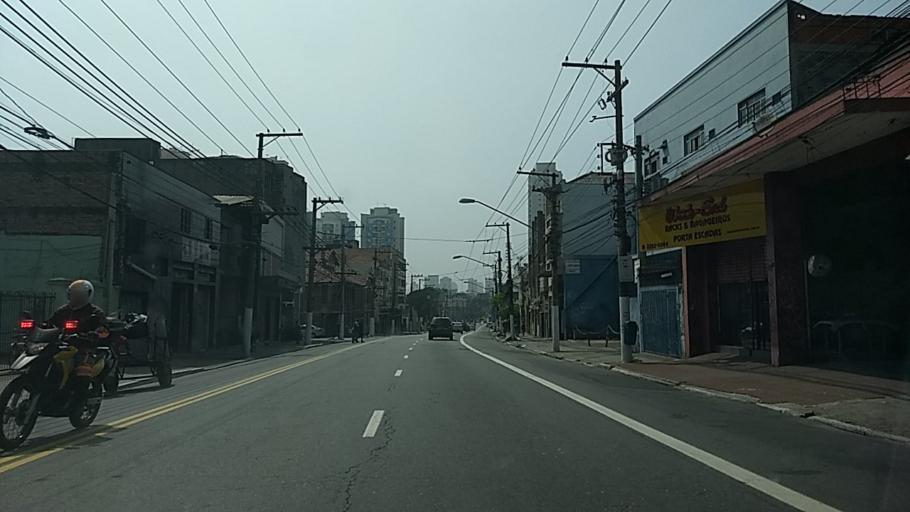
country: BR
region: Sao Paulo
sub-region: Sao Paulo
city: Sao Paulo
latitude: -23.5373
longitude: -46.5954
